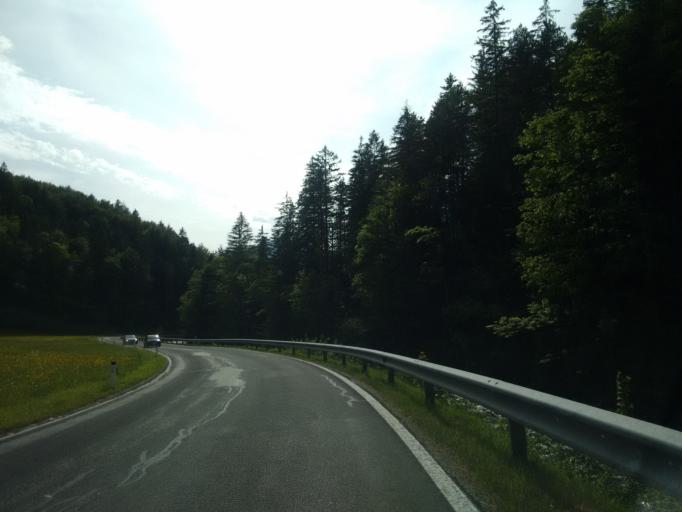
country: AT
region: Styria
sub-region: Politischer Bezirk Liezen
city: Bad Aussee
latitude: 47.6177
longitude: 13.8045
